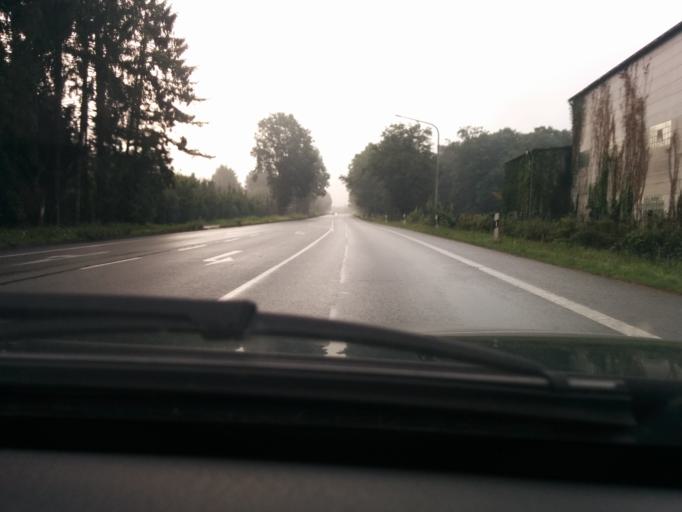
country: DE
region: North Rhine-Westphalia
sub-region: Regierungsbezirk Detmold
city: Steinhagen
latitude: 52.0223
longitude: 8.4240
